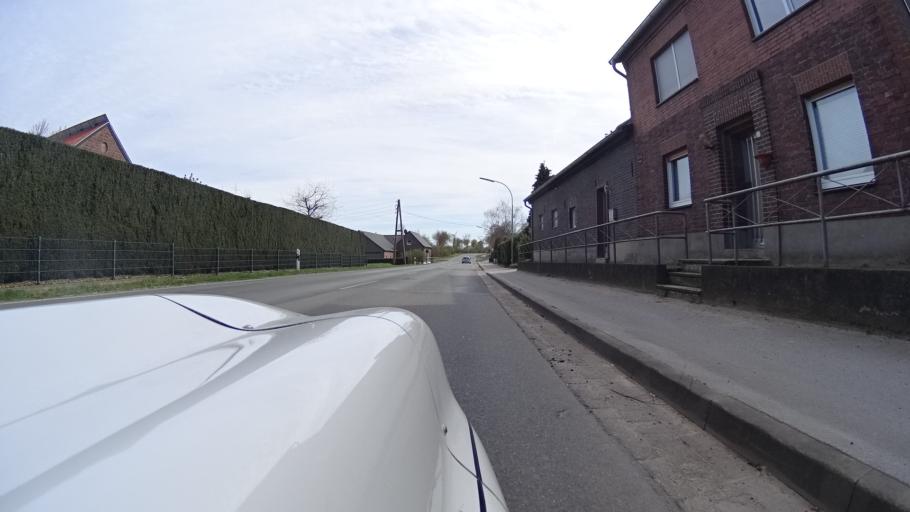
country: DE
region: North Rhine-Westphalia
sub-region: Regierungsbezirk Dusseldorf
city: Kevelaer
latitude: 51.5610
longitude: 6.2004
